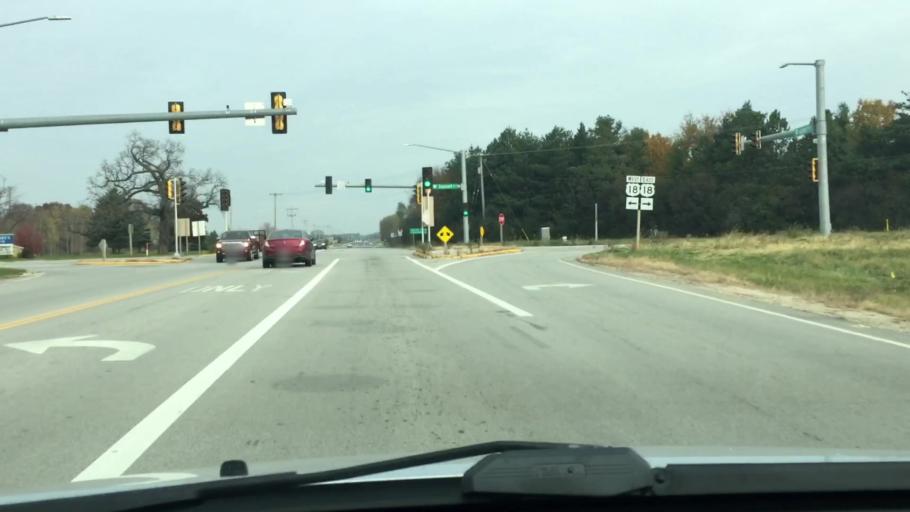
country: US
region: Wisconsin
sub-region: Waukesha County
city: Dousman
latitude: 43.0220
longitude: -88.4624
